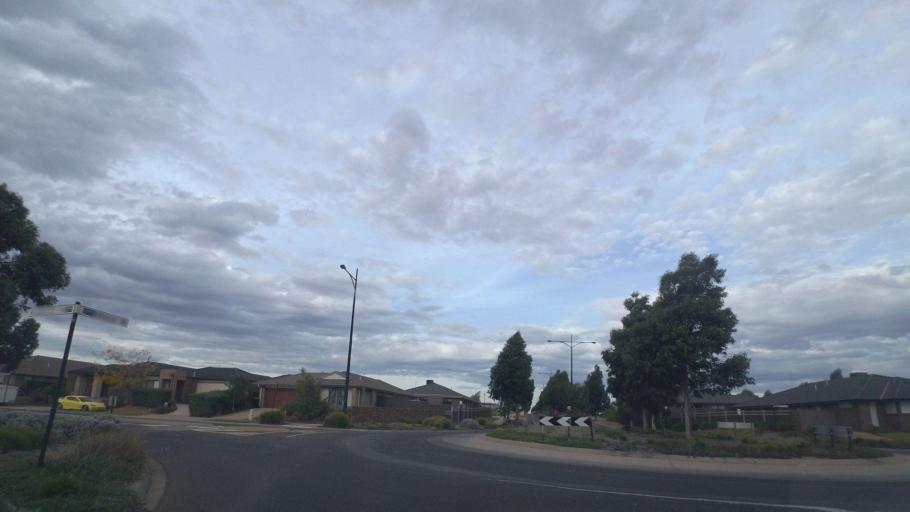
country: AU
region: Victoria
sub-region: Melton
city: Melton South
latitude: -37.7153
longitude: 144.5902
